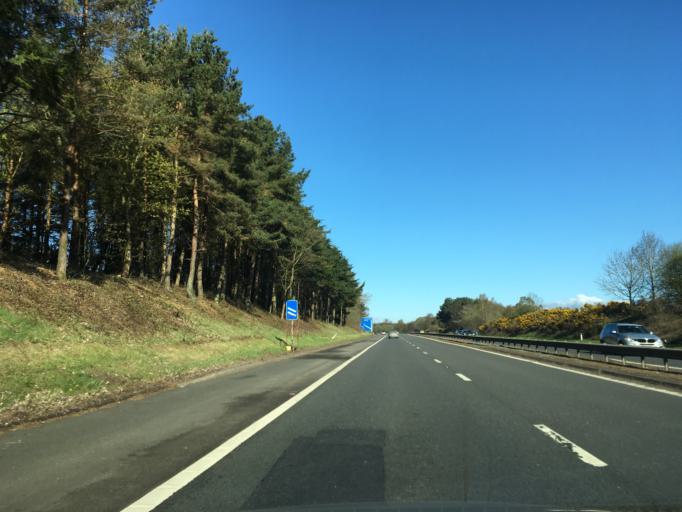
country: GB
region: Scotland
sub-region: Stirling
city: Bannockburn
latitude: 56.0726
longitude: -3.9058
